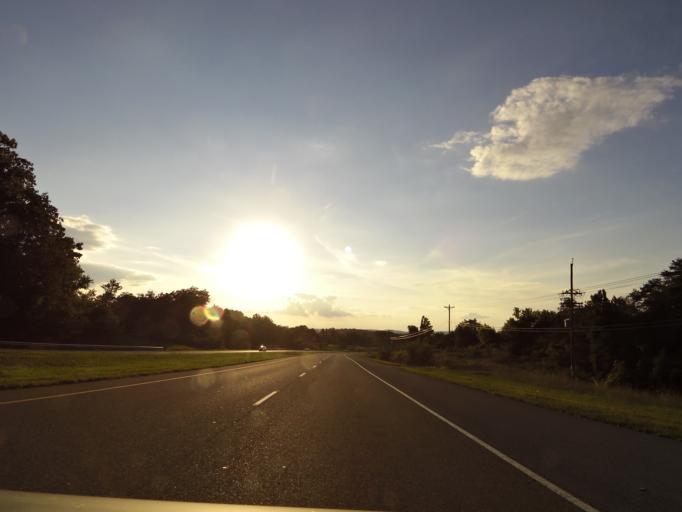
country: US
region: Tennessee
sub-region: Loudon County
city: Lenoir City
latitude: 35.7587
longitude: -84.2224
